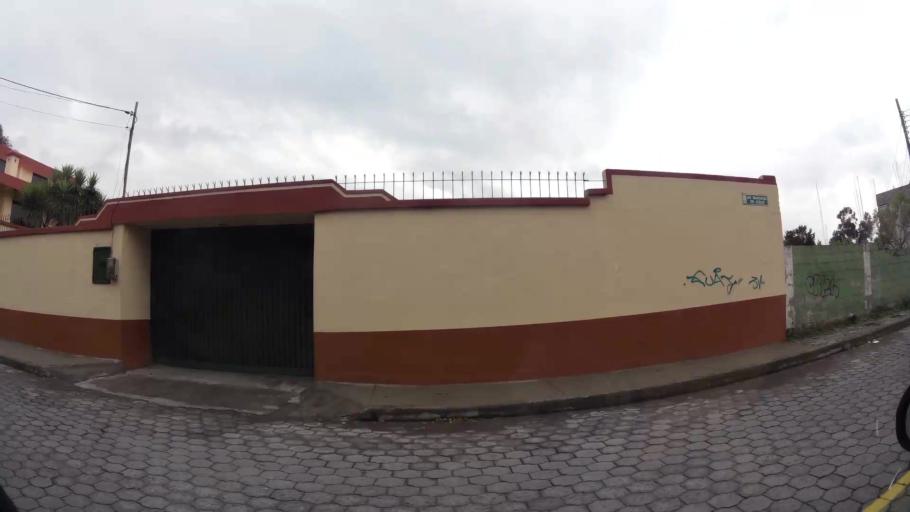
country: EC
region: Pichincha
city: Sangolqui
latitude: -0.3033
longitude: -78.4609
